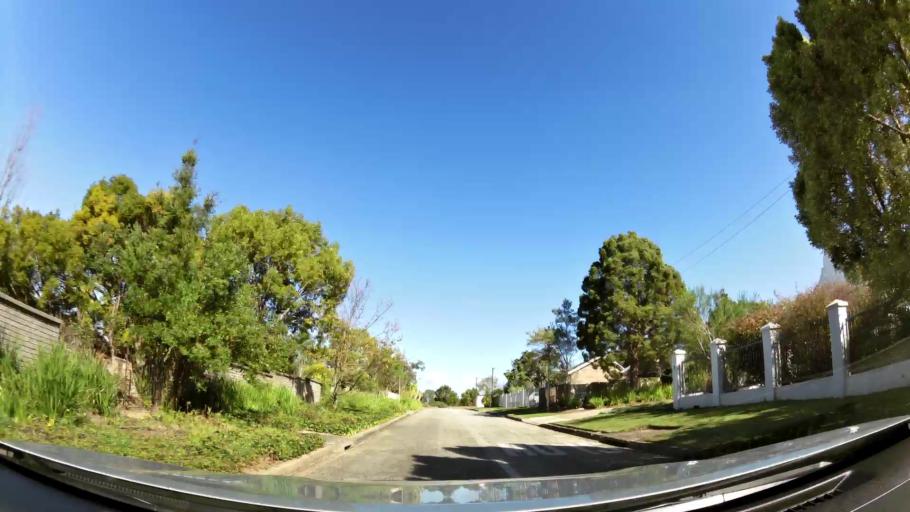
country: ZA
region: Western Cape
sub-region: Eden District Municipality
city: George
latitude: -33.9447
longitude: 22.4662
